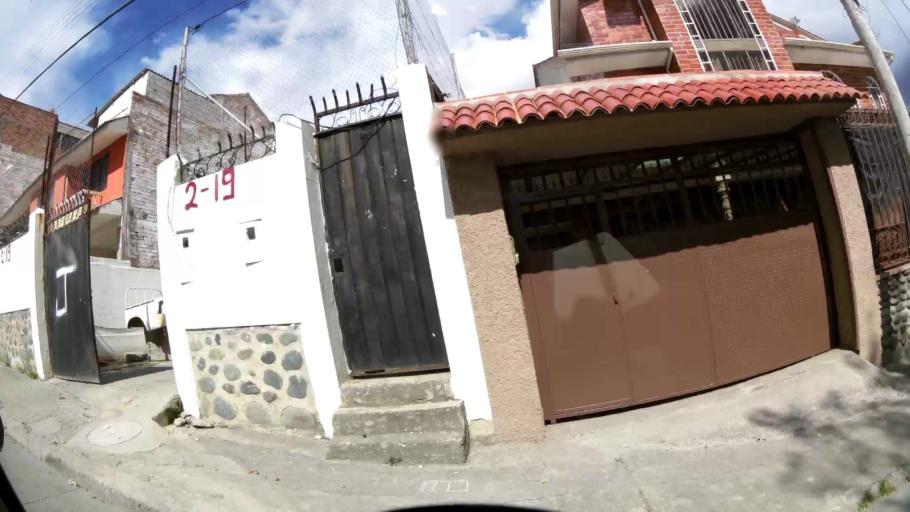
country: EC
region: Azuay
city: Cuenca
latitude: -2.8886
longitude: -78.9971
